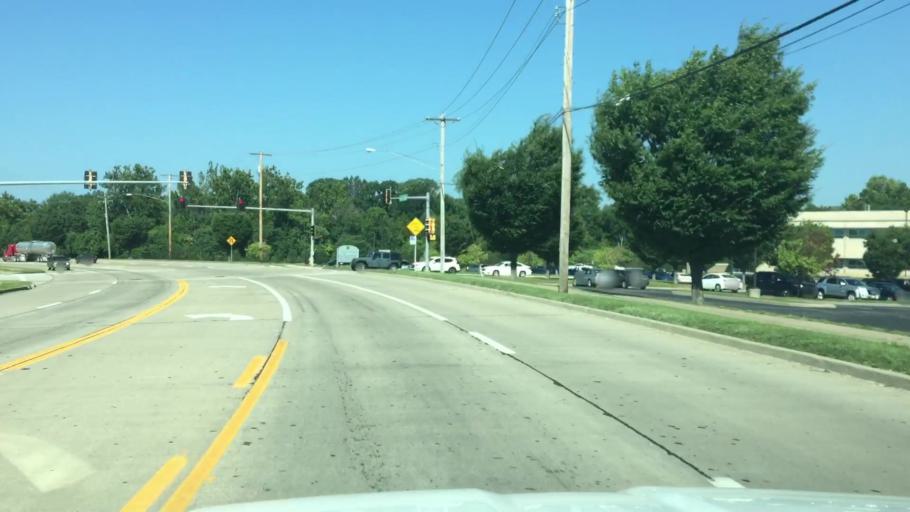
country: US
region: Missouri
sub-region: Jefferson County
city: Arnold
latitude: 38.4651
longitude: -90.3582
